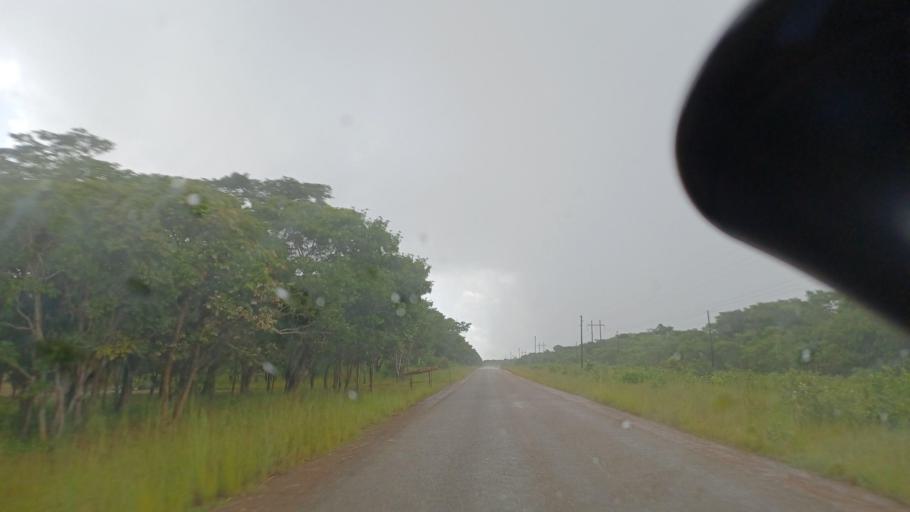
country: ZM
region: North-Western
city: Kasempa
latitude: -13.0913
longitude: 25.9352
